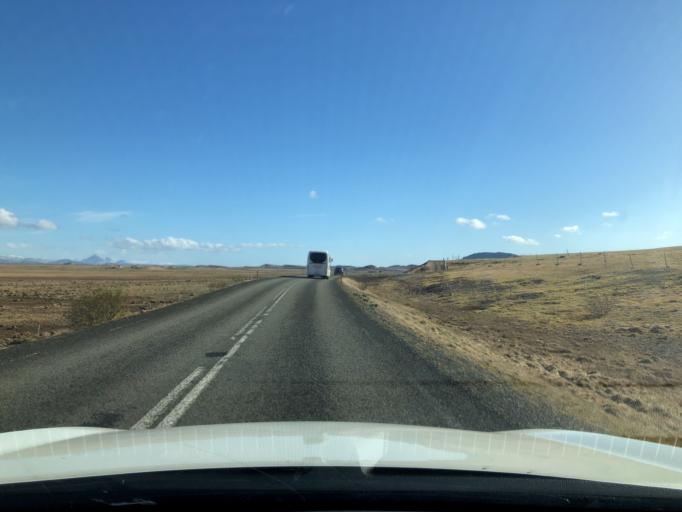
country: IS
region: West
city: Borgarnes
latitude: 64.5375
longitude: -21.7625
